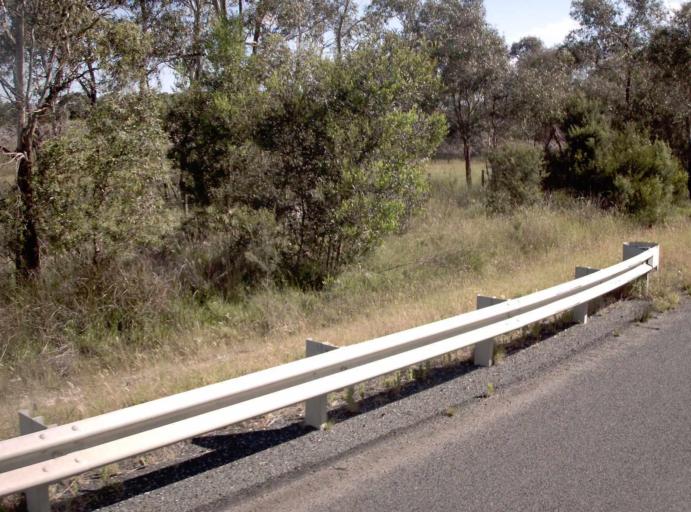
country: AU
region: Victoria
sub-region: Bass Coast
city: North Wonthaggi
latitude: -38.4368
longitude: 145.4901
